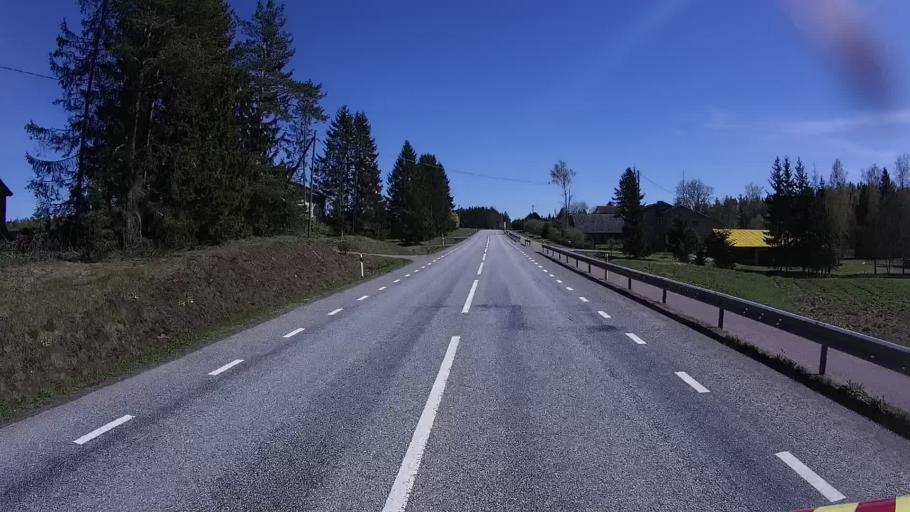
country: EE
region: Laeaene-Virumaa
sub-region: Tapa vald
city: Tapa
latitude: 59.2563
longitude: 25.6673
